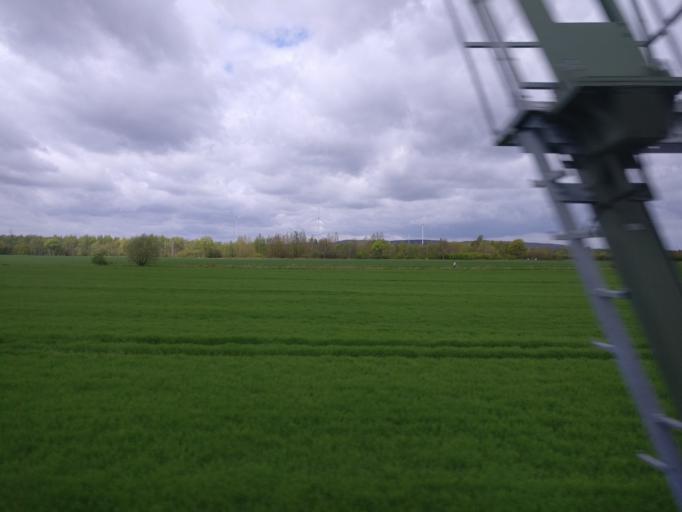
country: DE
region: Lower Saxony
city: Vienenburg
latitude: 51.9298
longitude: 10.5170
